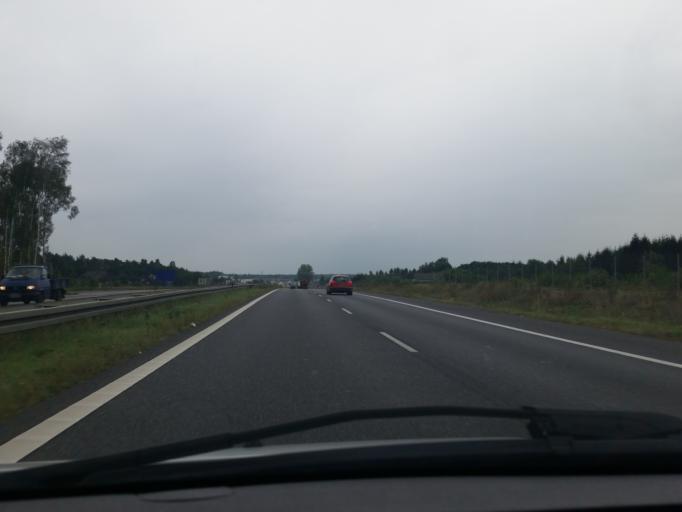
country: PL
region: Masovian Voivodeship
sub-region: Powiat zyrardowski
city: Mszczonow
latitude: 51.9505
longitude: 20.4900
